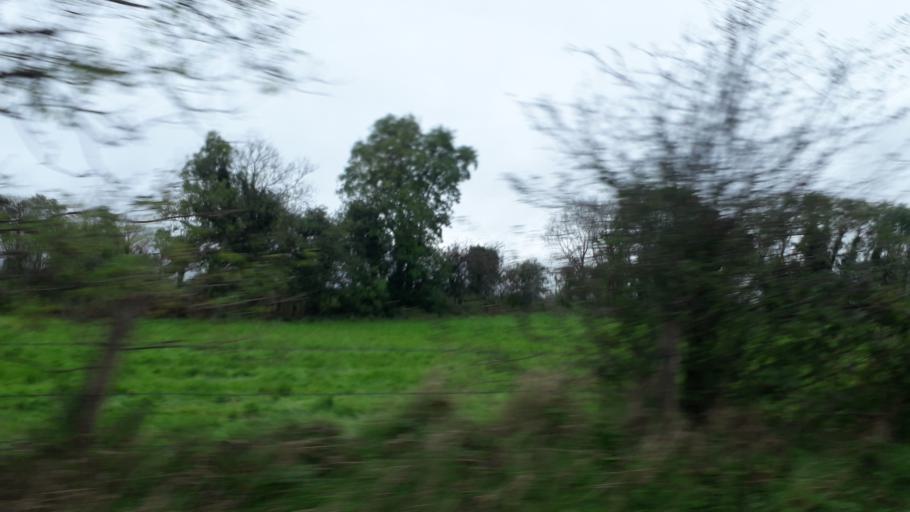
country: IE
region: Connaught
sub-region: Roscommon
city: Ballaghaderreen
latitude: 53.8936
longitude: -8.5570
